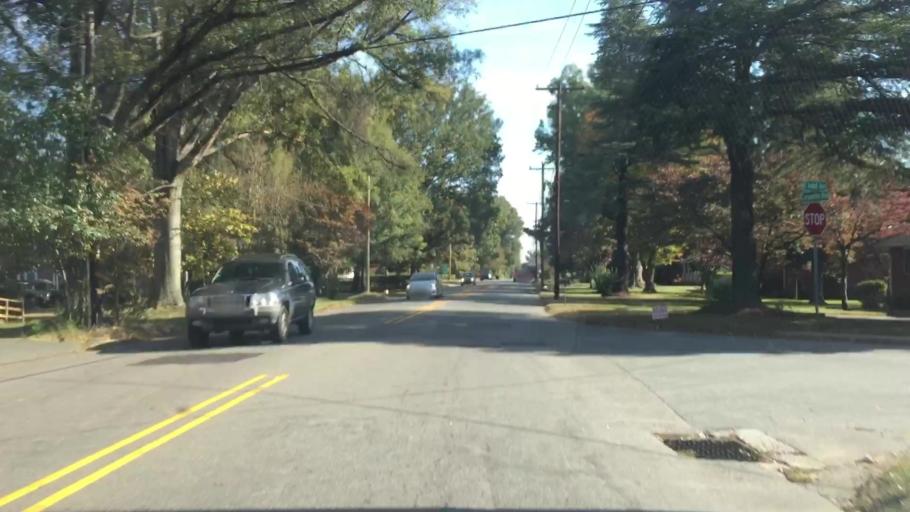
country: US
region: North Carolina
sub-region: Iredell County
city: Mooresville
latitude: 35.5810
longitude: -80.7964
